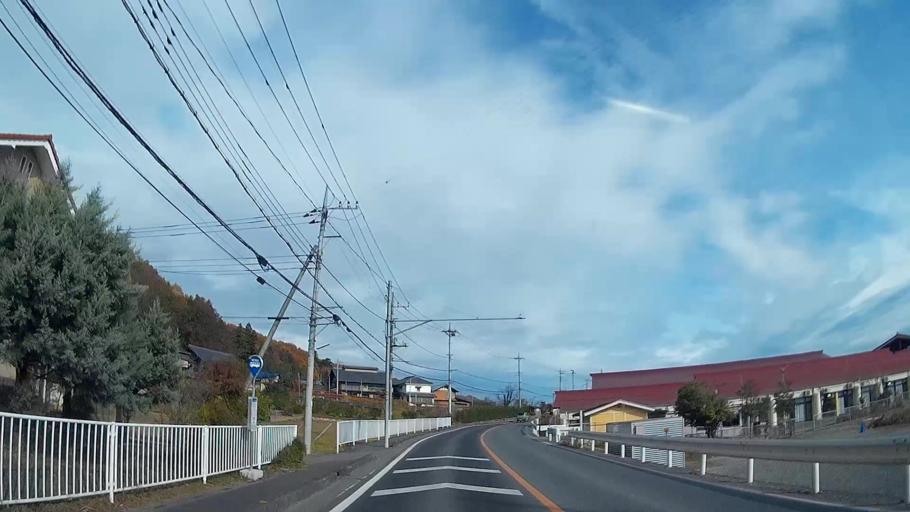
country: JP
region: Saitama
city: Chichibu
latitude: 36.0050
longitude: 139.0686
